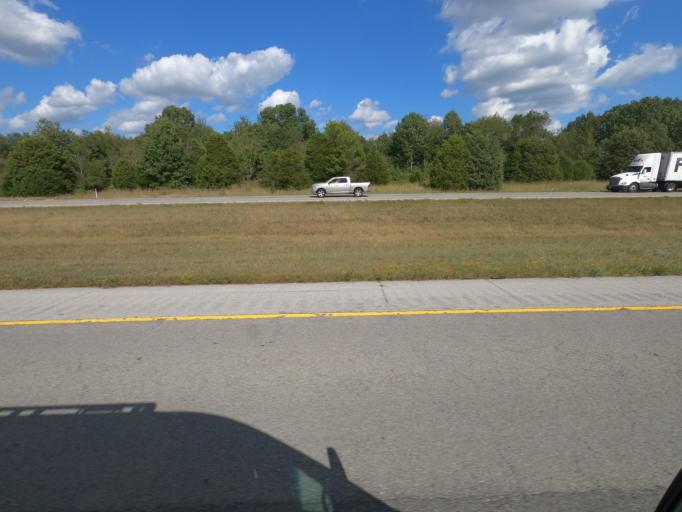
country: US
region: Illinois
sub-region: Johnson County
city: Vienna
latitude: 37.3311
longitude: -88.7748
